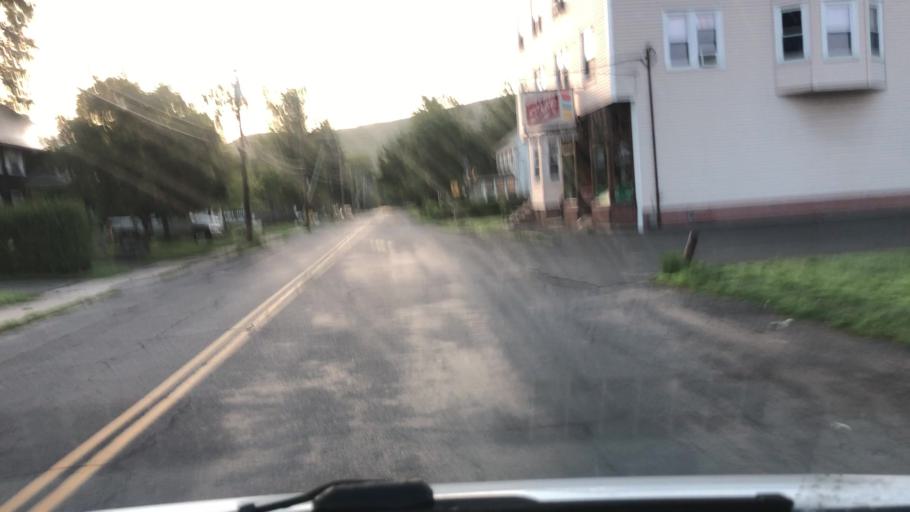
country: US
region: Massachusetts
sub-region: Hampshire County
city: Easthampton
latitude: 42.2757
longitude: -72.6521
